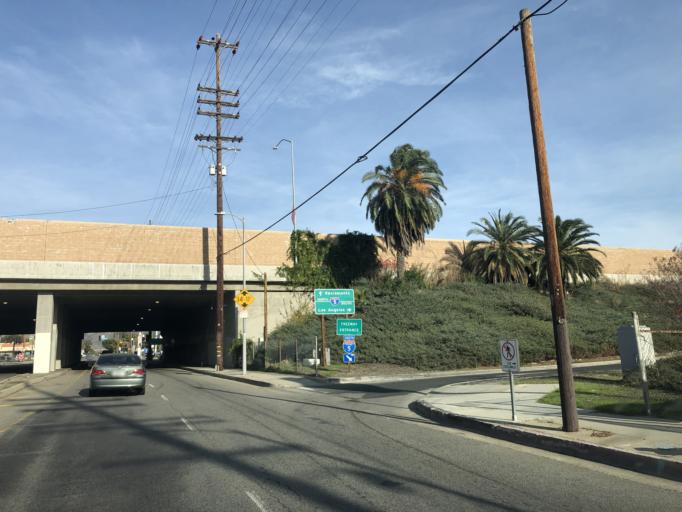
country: US
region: California
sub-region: Los Angeles County
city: San Fernando
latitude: 34.2763
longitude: -118.4536
